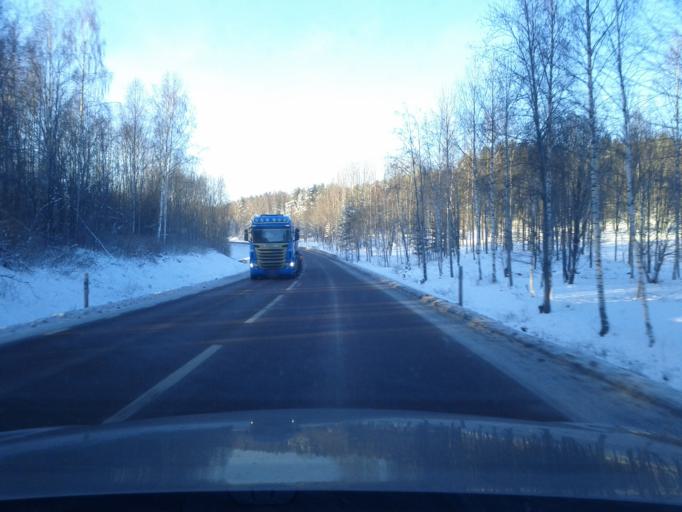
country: SE
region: Dalarna
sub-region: Faluns Kommun
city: Falun
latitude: 60.6226
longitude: 15.6441
